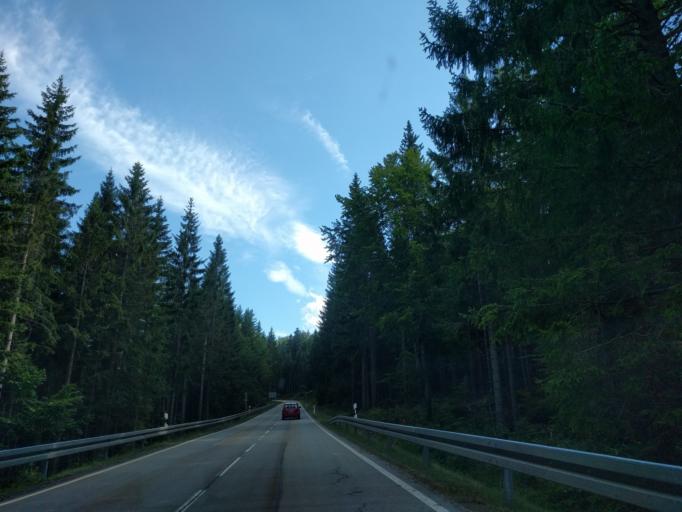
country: DE
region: Bavaria
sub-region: Lower Bavaria
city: Bayerisch Eisenstein
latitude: 49.0969
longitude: 13.1613
